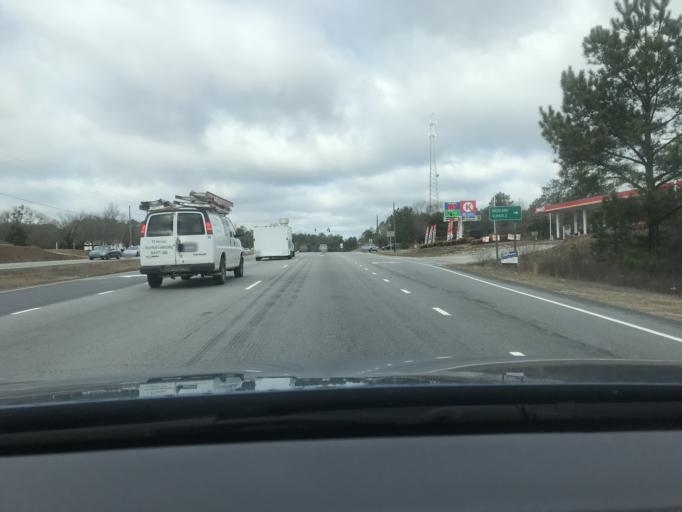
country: US
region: North Carolina
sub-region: Cumberland County
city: Spring Lake
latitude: 35.2746
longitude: -79.0680
